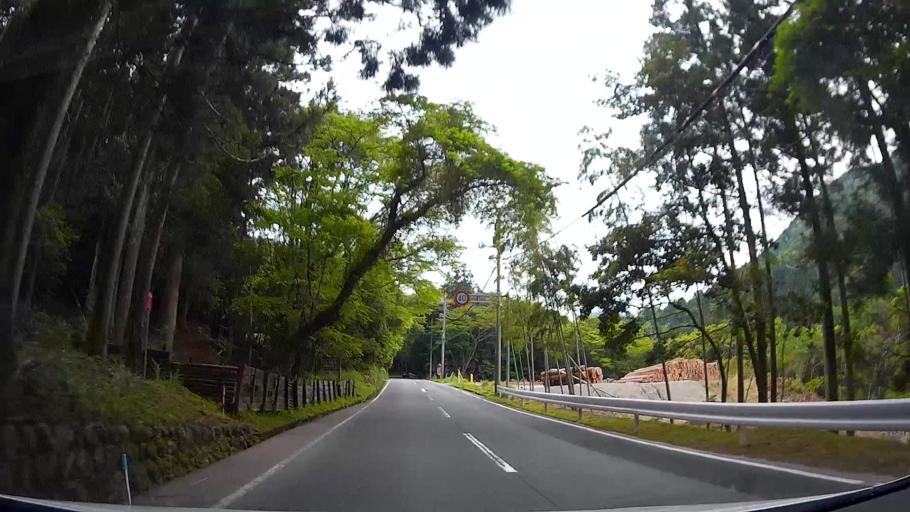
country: JP
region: Shizuoka
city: Heda
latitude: 34.8606
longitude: 138.9229
